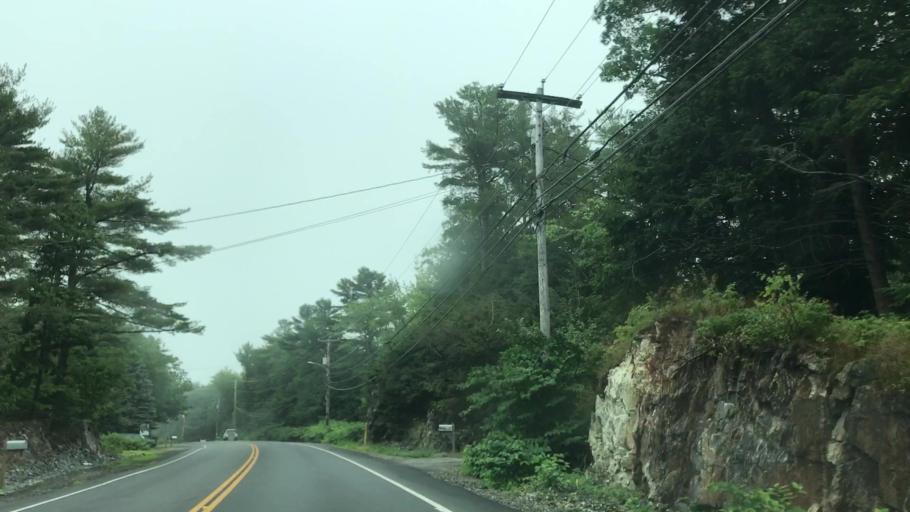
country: US
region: Maine
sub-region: Sagadahoc County
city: Bath
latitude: 43.9043
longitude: -69.8577
